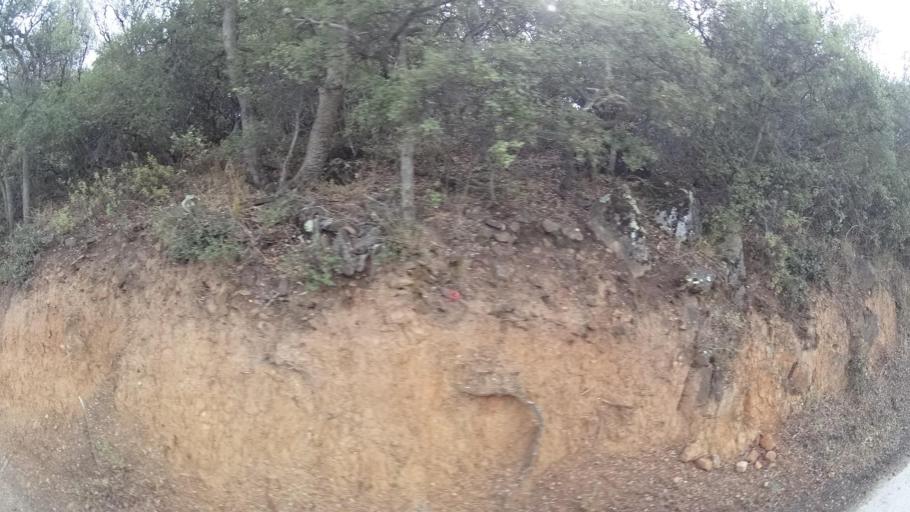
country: US
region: California
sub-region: San Diego County
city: Descanso
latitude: 32.8580
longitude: -116.6194
